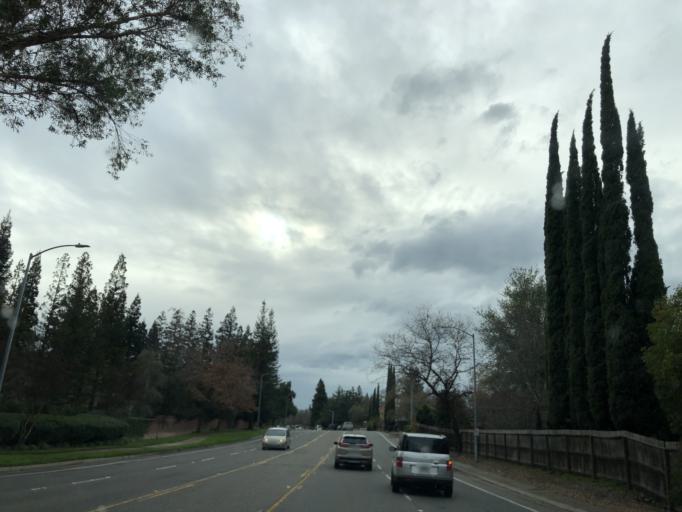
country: US
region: California
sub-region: Sacramento County
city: Carmichael
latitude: 38.6022
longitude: -121.3394
